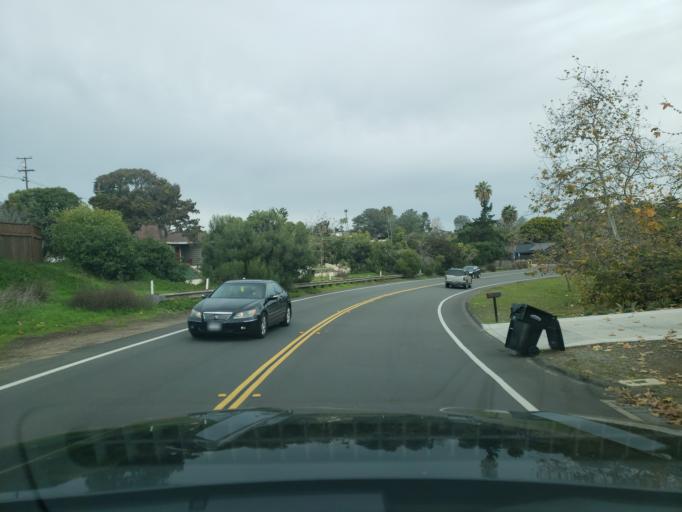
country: US
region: California
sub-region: San Diego County
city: Coronado
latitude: 32.7270
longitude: -117.2414
